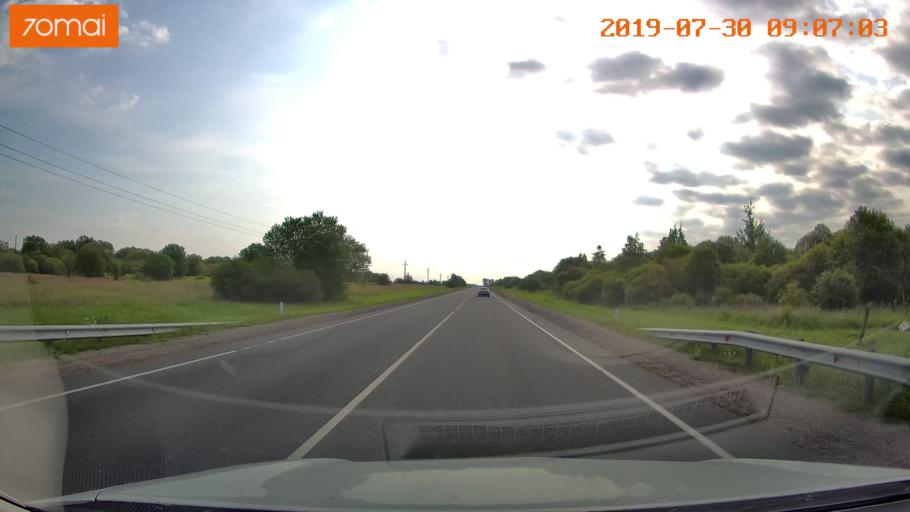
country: RU
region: Kaliningrad
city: Gusev
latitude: 54.6107
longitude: 22.3530
